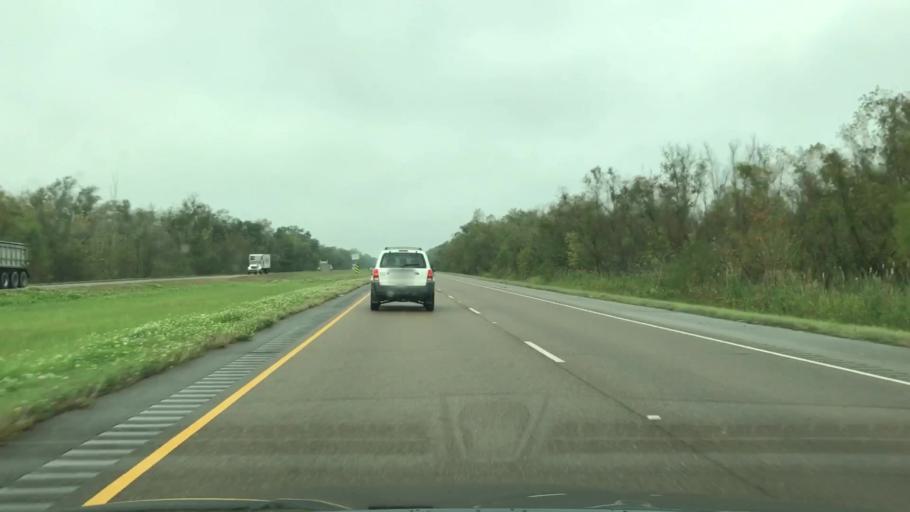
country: US
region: Louisiana
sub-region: Terrebonne Parish
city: Bayou Cane
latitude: 29.6861
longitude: -90.7140
